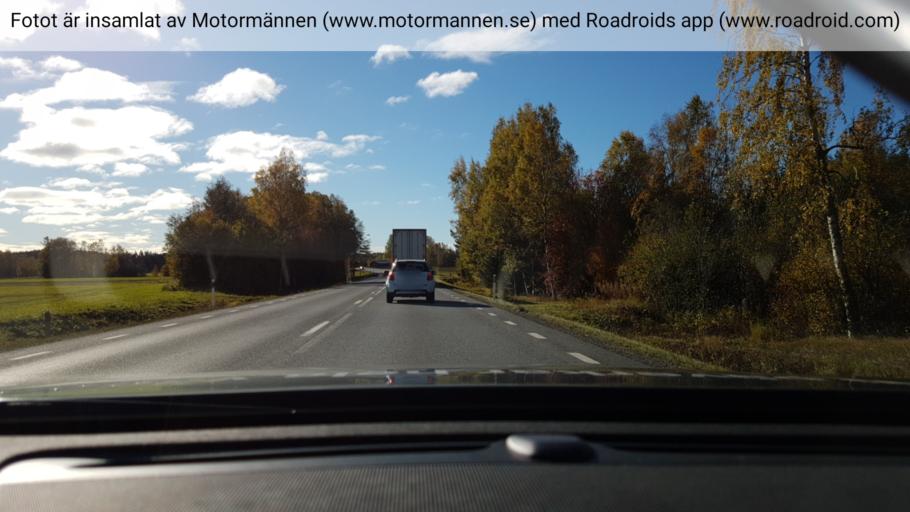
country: SE
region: Vaesterbotten
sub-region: Skelleftea Kommun
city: Burea
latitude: 64.5129
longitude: 21.2572
